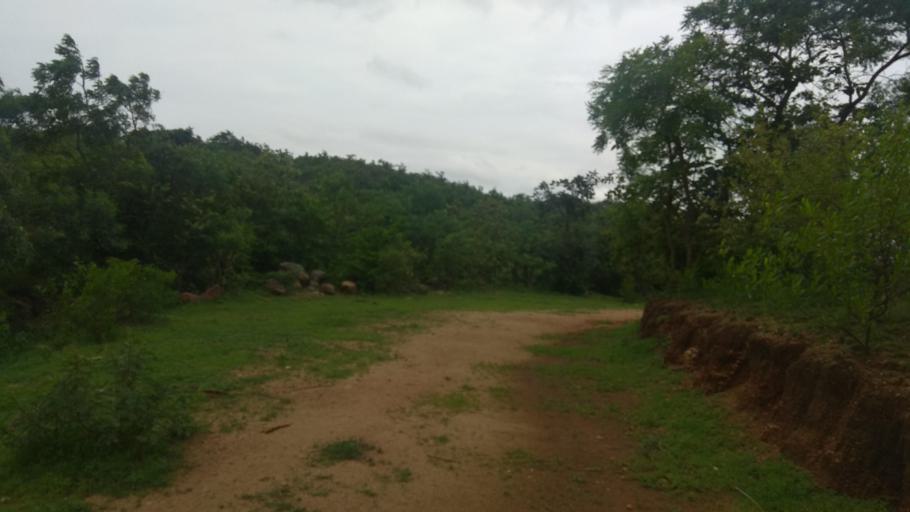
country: IN
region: Telangana
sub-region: Mahbubnagar
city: Farrukhnagar
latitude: 16.8915
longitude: 78.4973
